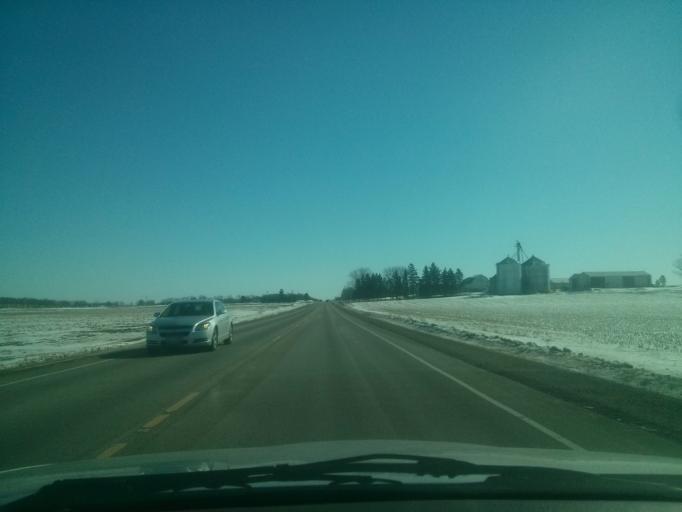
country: US
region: Wisconsin
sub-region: Saint Croix County
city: New Richmond
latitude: 45.1371
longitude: -92.4723
